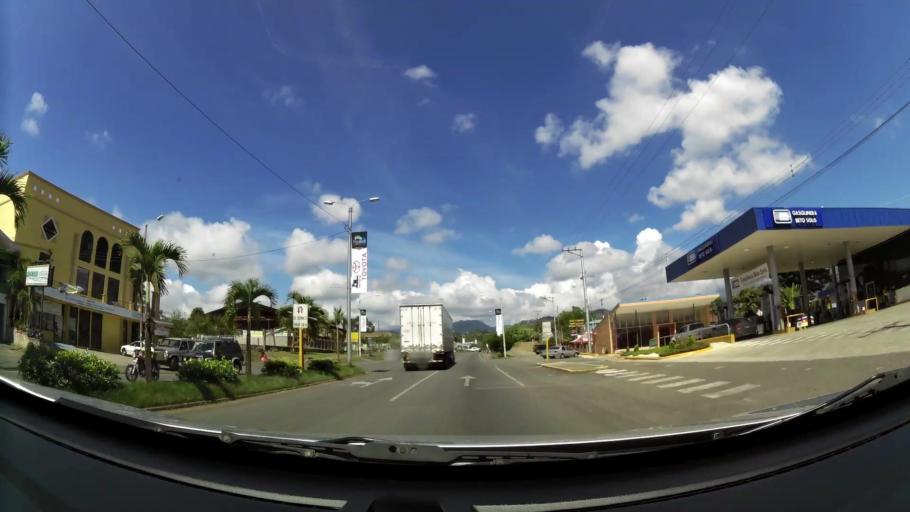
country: CR
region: San Jose
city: San Isidro
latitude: 9.3781
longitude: -83.7042
